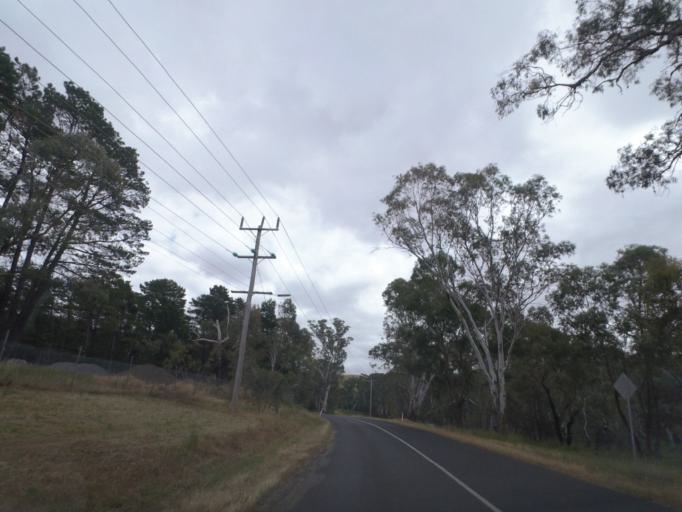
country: AU
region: Victoria
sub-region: Whittlesea
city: Whittlesea
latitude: -37.2001
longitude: 145.0405
